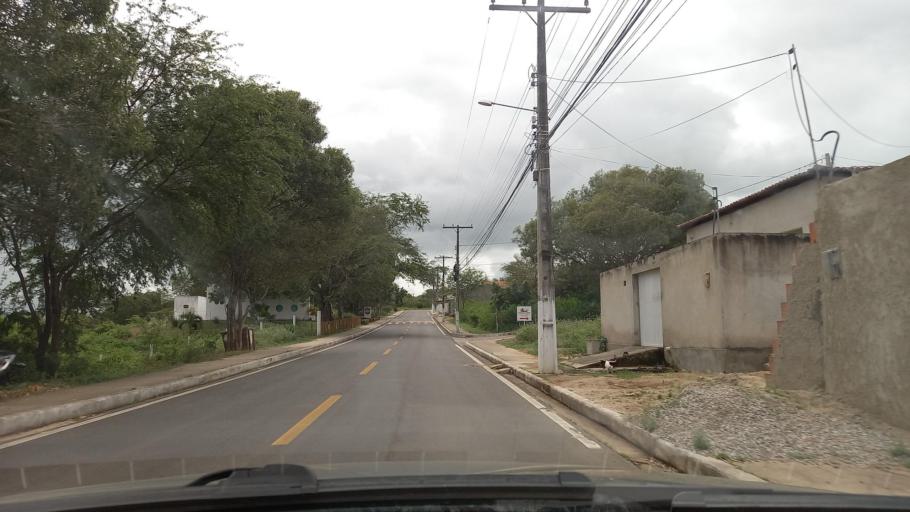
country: BR
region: Sergipe
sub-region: Caninde De Sao Francisco
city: Caninde de Sao Francisco
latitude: -9.6202
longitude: -37.7661
